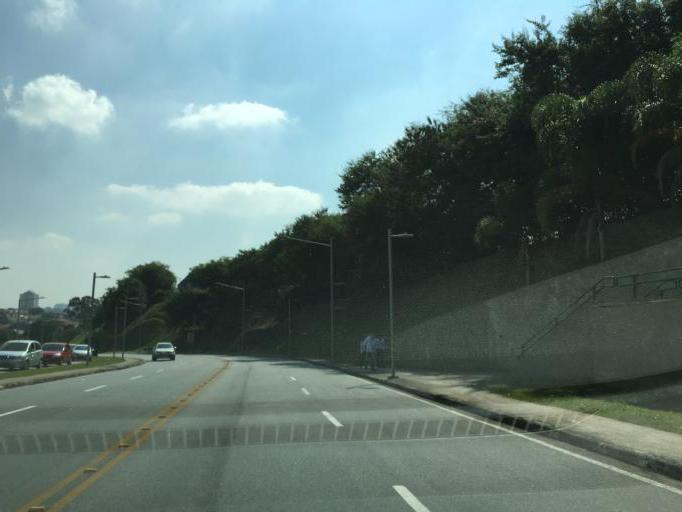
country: BR
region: Sao Paulo
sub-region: Osasco
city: Osasco
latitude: -23.5691
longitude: -46.7377
